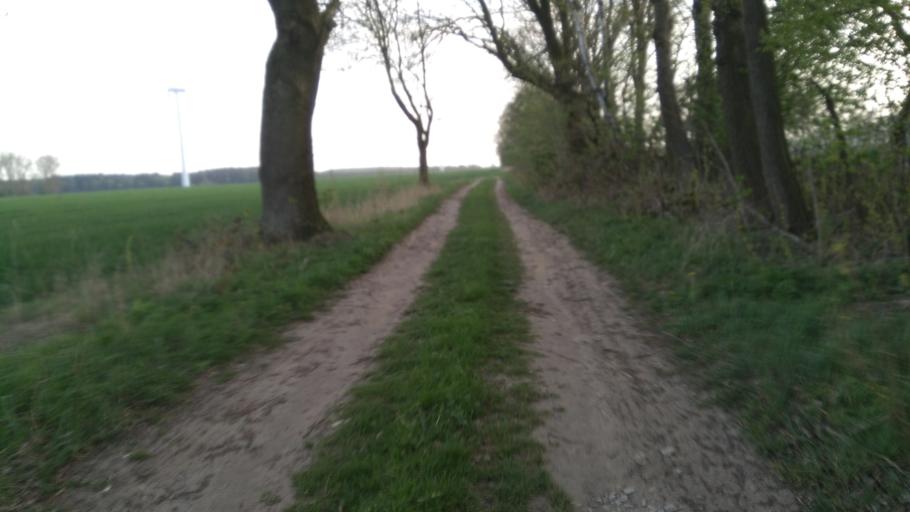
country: DE
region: Lower Saxony
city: Nottensdorf
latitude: 53.4555
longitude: 9.5993
